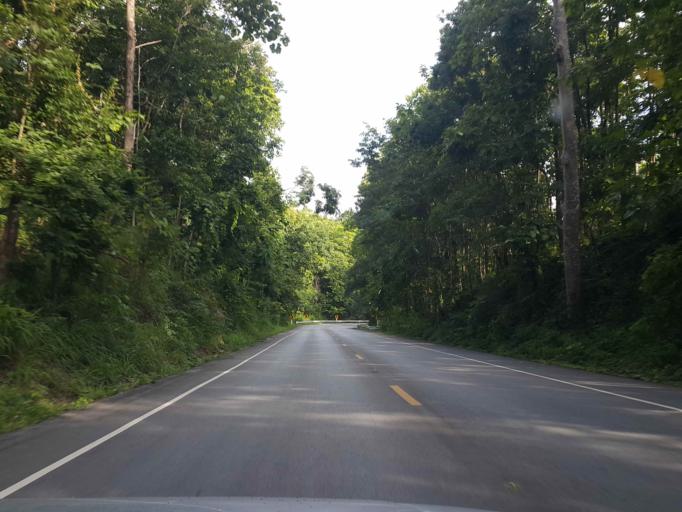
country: TH
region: Phrae
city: Den Chai
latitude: 17.8258
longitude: 99.8647
